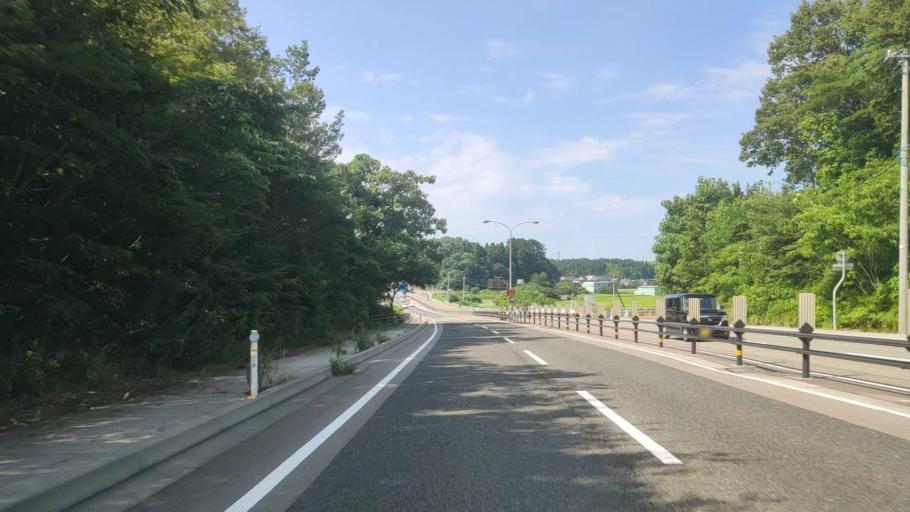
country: JP
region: Ishikawa
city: Komatsu
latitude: 36.4273
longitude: 136.5318
